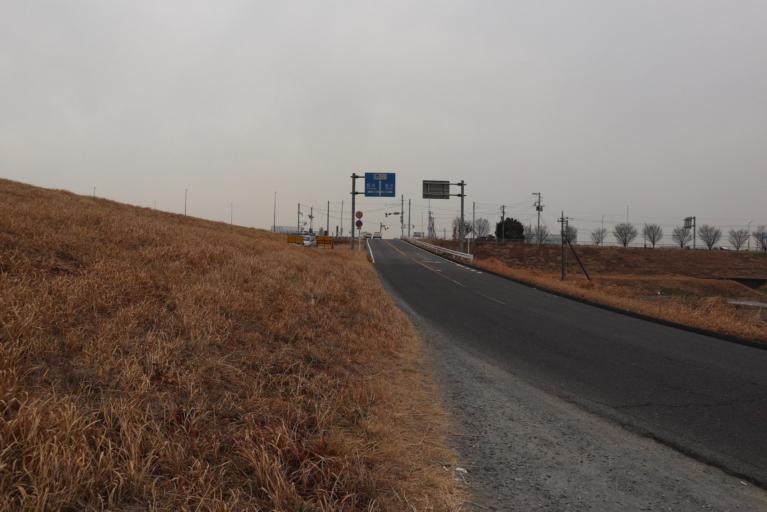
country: JP
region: Saitama
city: Hanyu
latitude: 36.1899
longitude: 139.5084
